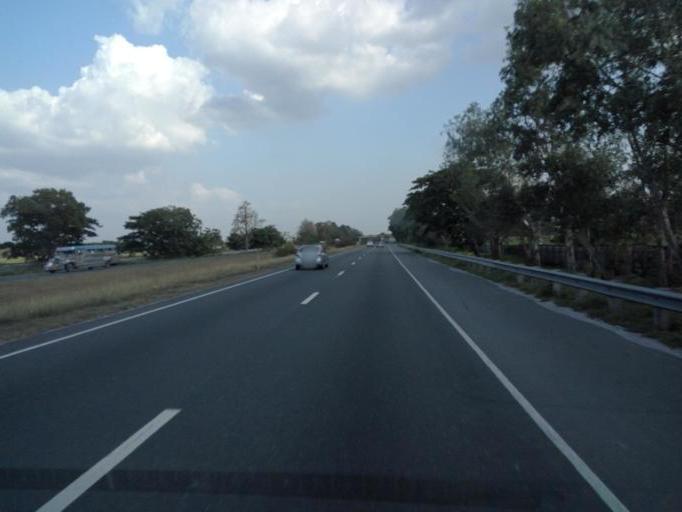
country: PH
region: Central Luzon
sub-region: Province of Pampanga
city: Acli
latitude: 15.1261
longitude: 120.6475
